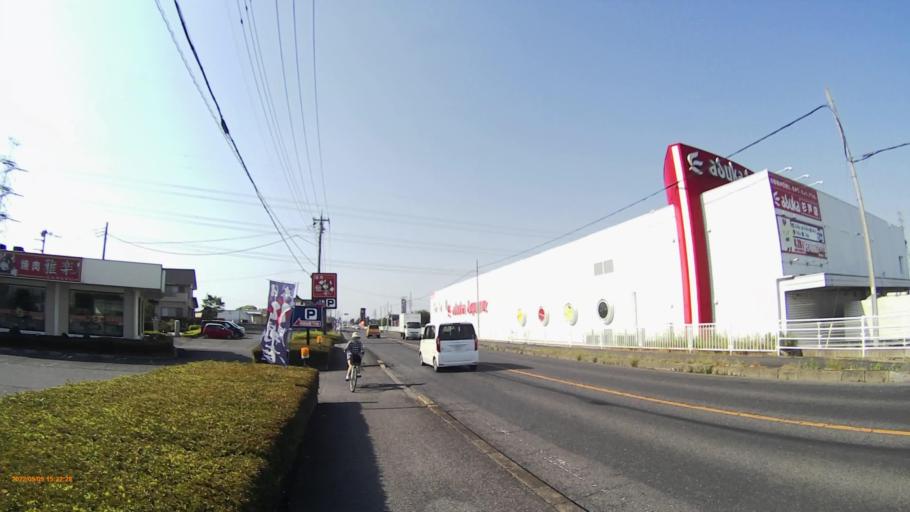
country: JP
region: Saitama
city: Sugito
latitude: 36.0387
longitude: 139.7219
